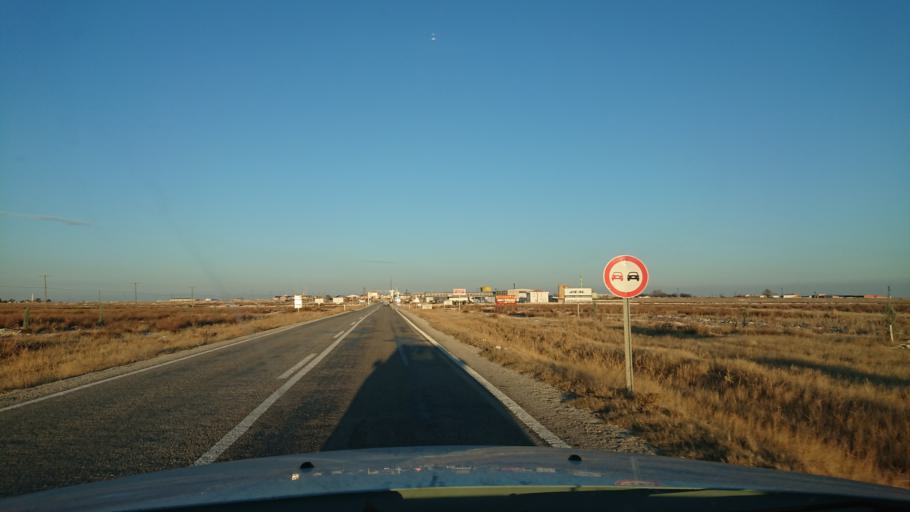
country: TR
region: Aksaray
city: Eskil
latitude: 38.3907
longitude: 33.3886
